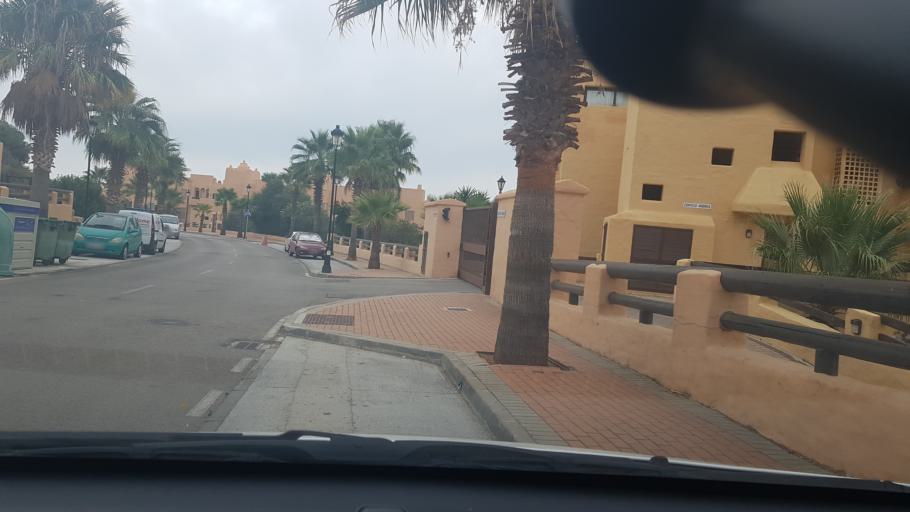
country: ES
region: Andalusia
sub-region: Provincia de Malaga
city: Manilva
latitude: 36.3651
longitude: -5.2396
